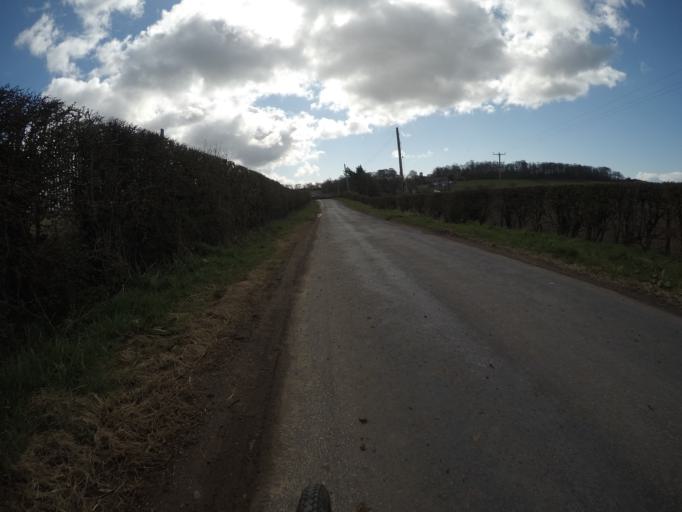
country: GB
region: Scotland
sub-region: South Ayrshire
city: Dundonald
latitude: 55.5872
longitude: -4.5764
